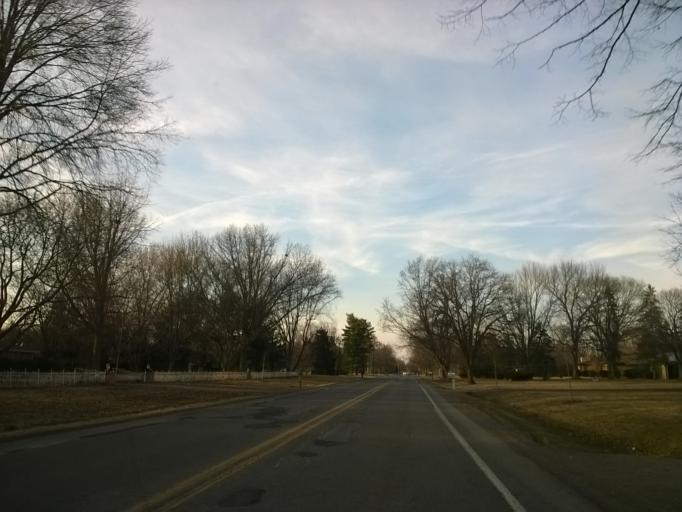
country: US
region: Indiana
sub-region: Marion County
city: Meridian Hills
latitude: 39.8477
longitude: -86.2119
